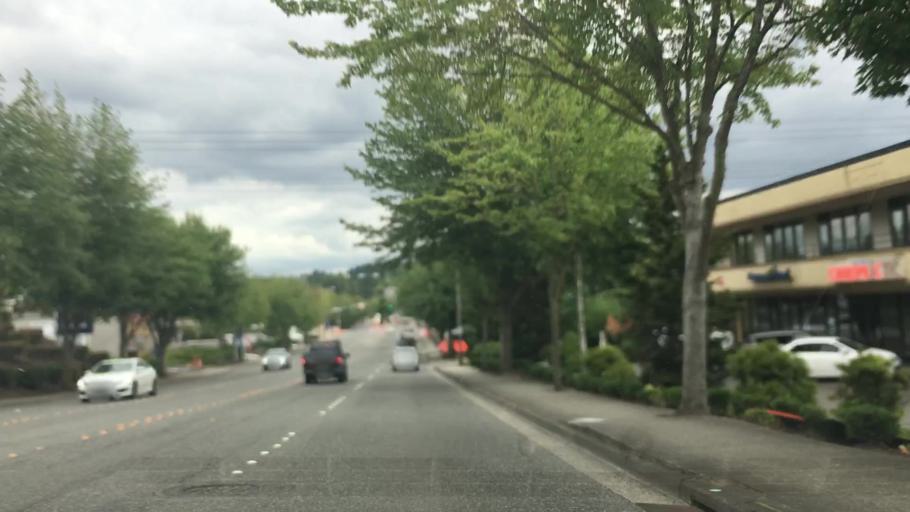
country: US
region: Washington
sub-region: King County
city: Bellevue
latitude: 47.6279
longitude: -122.1602
